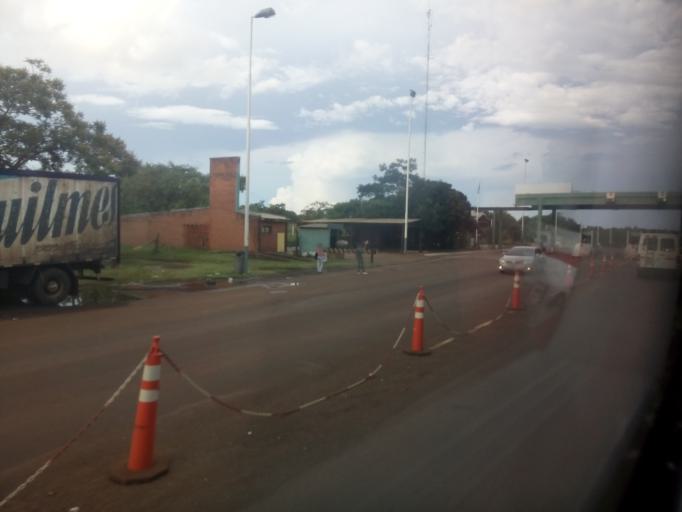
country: AR
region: Misiones
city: Santa Ana
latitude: -27.4290
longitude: -55.6303
